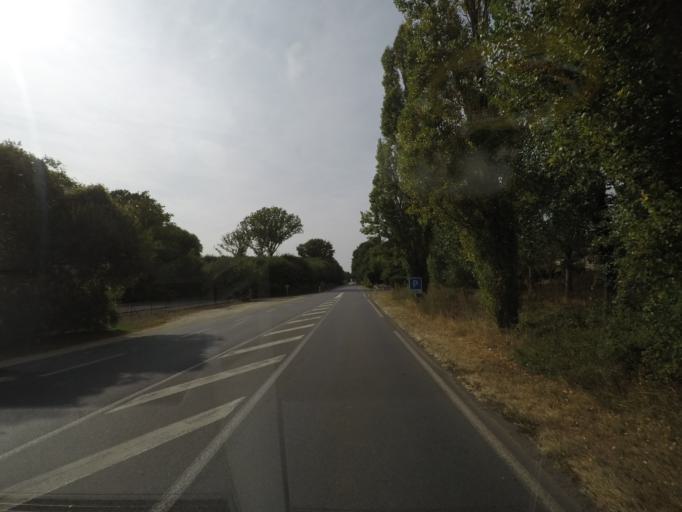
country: FR
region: Poitou-Charentes
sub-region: Departement des Deux-Sevres
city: Chef-Boutonne
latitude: 46.1821
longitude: -0.0294
